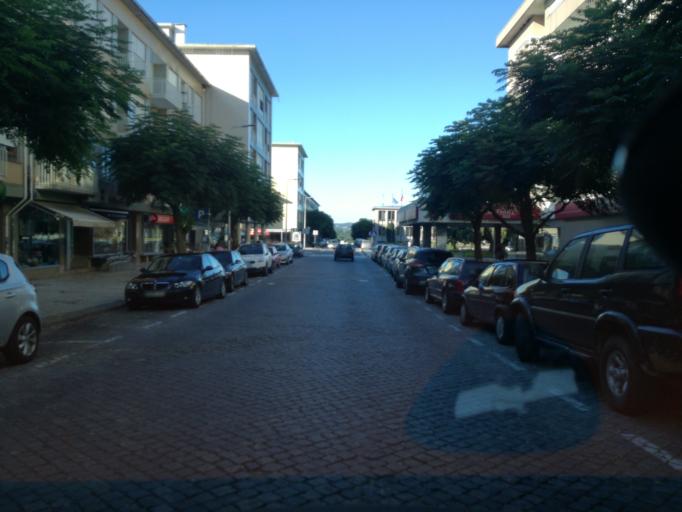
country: PT
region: Porto
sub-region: Santo Tirso
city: Santo Tirso
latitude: 41.3408
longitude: -8.4743
